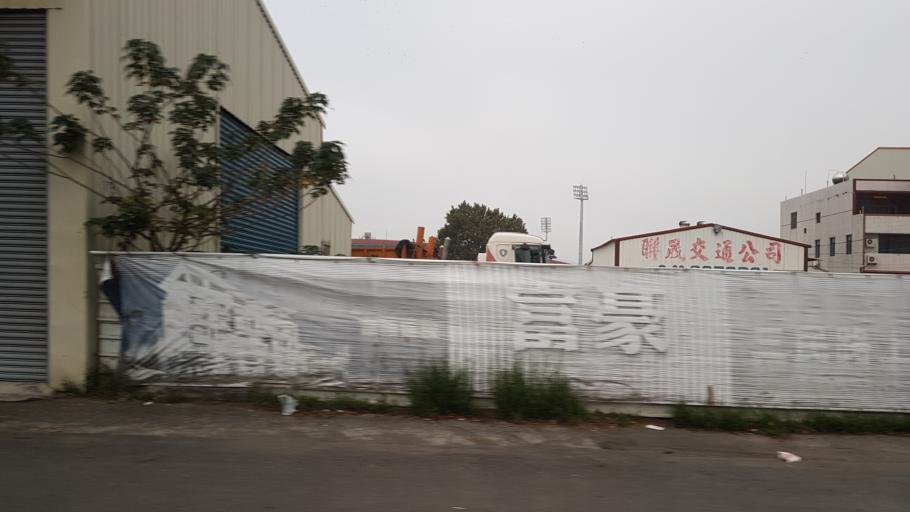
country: TW
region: Taiwan
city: Xinying
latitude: 23.3212
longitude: 120.3162
